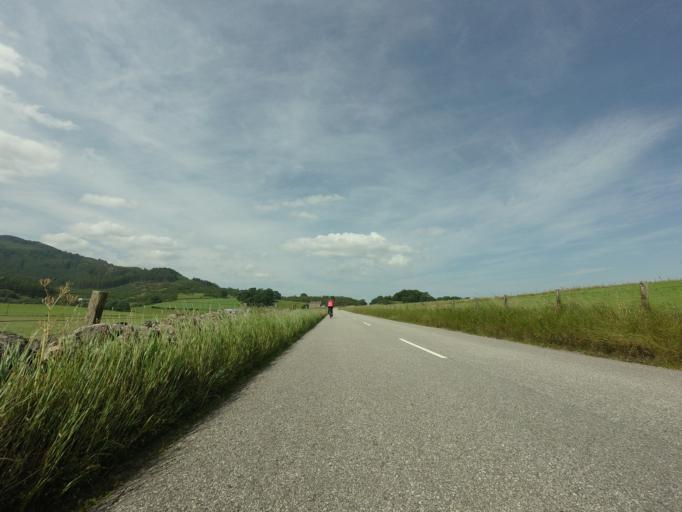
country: GB
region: Scotland
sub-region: Highland
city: Tain
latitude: 57.8469
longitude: -4.2003
